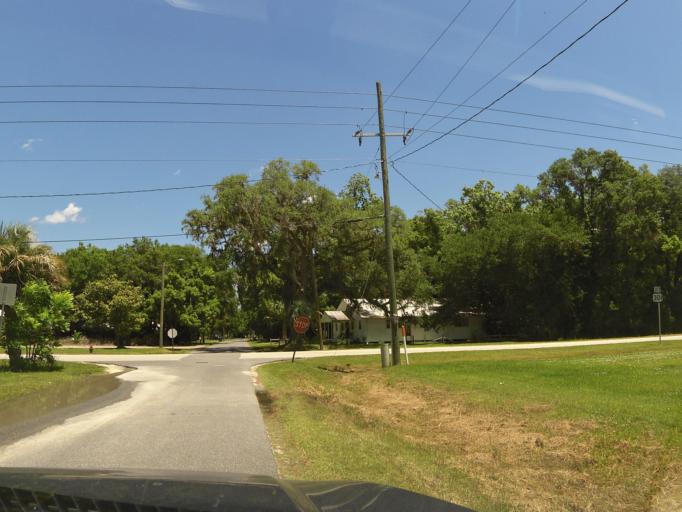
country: US
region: Florida
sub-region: Bradford County
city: Starke
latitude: 30.0432
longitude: -82.0739
